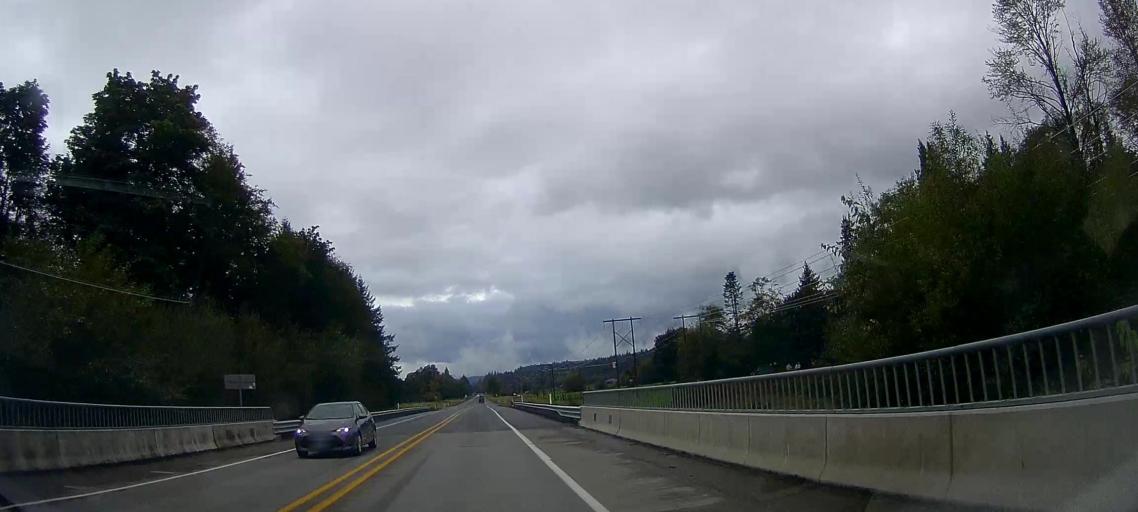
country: US
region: Washington
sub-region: Skagit County
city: Sedro-Woolley
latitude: 48.5297
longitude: -122.0251
